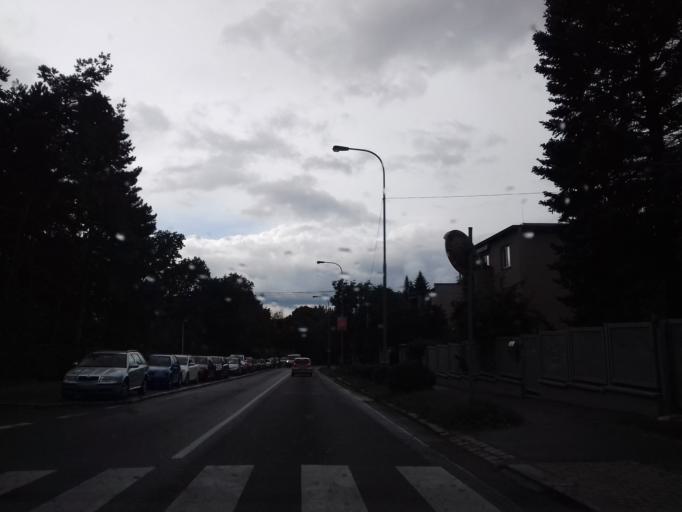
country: CZ
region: Praha
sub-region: Praha 4
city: Hodkovicky
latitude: 50.0254
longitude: 14.4228
